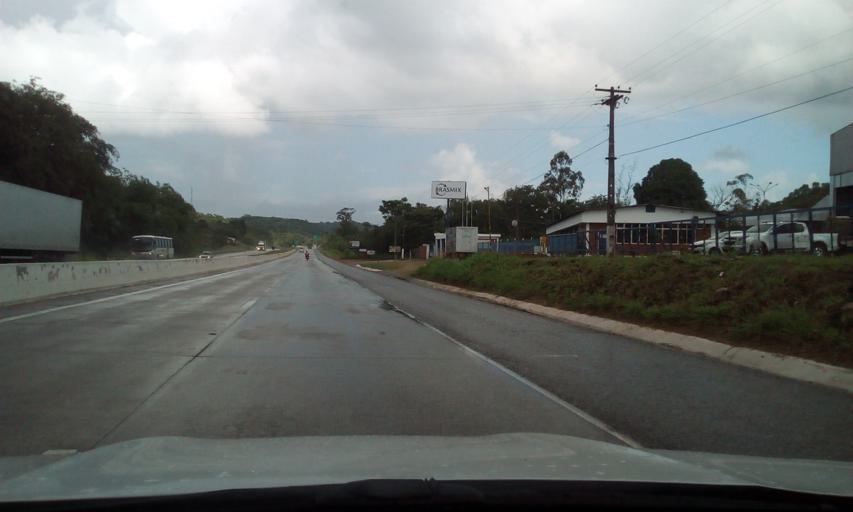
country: BR
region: Pernambuco
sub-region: Cabo De Santo Agostinho
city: Cabo
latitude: -8.3090
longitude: -35.0862
